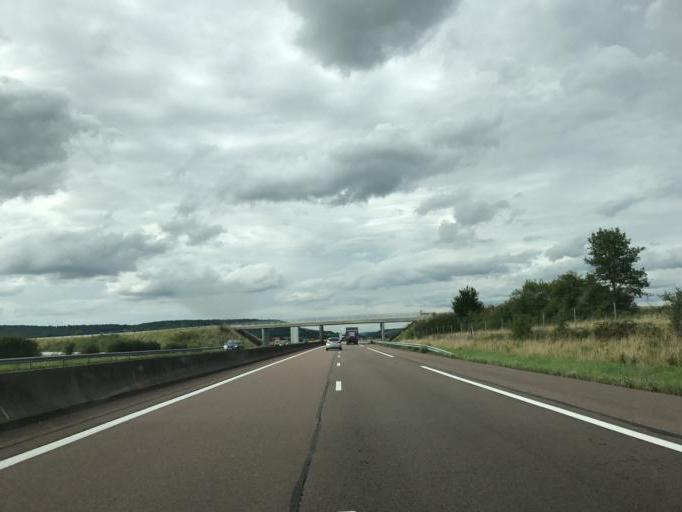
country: FR
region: Bourgogne
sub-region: Departement de la Cote-d'Or
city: Pouilly-en-Auxois
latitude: 47.2726
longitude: 4.5125
